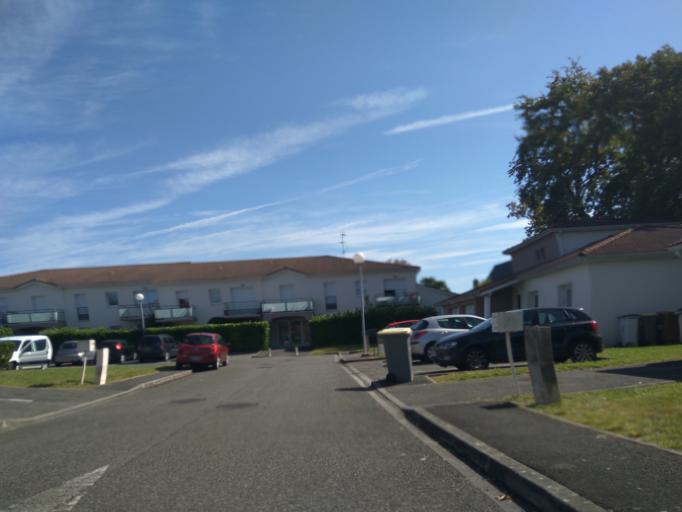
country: FR
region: Aquitaine
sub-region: Departement des Pyrenees-Atlantiques
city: Pau
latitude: 43.3125
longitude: -0.3400
